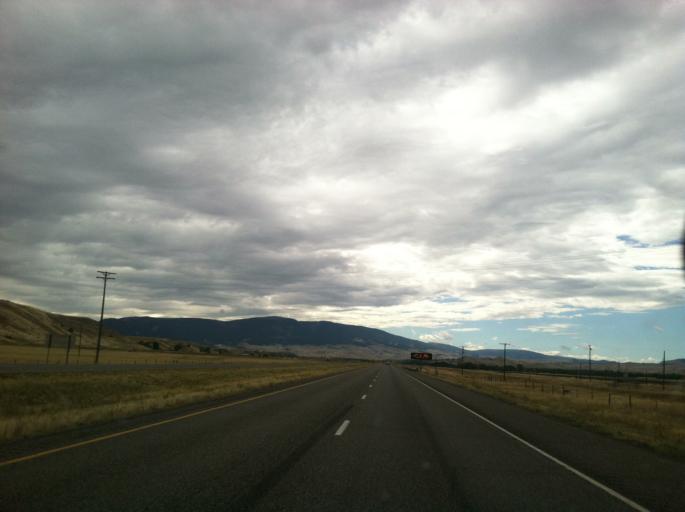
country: US
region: Montana
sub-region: Park County
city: Livingston
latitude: 45.6948
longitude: -110.4854
